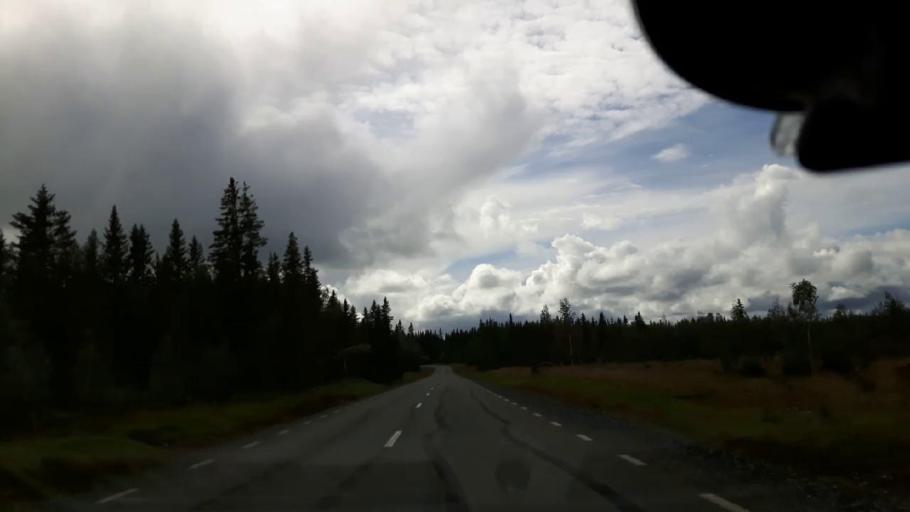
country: SE
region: Jaemtland
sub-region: Krokoms Kommun
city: Valla
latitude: 63.4706
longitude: 13.8369
